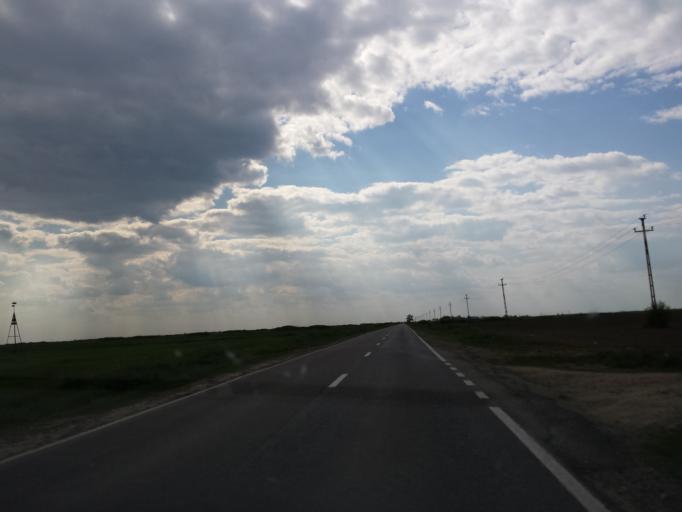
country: RO
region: Timis
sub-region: Comuna Cenad
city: Cenad
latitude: 46.1295
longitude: 20.5370
